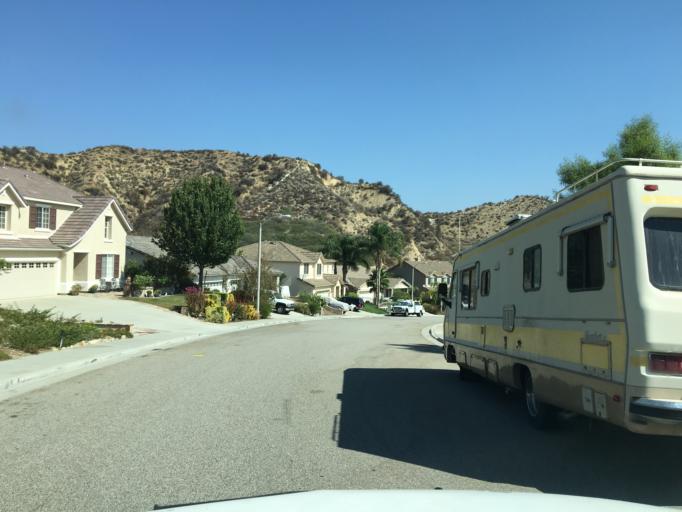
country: US
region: California
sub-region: Los Angeles County
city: Castaic
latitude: 34.4854
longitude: -118.6289
